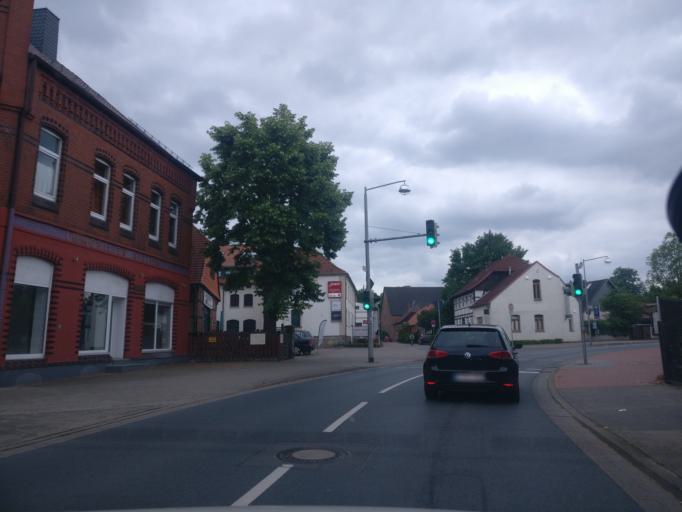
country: DE
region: Lower Saxony
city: Laatzen
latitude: 52.3425
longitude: 9.8271
